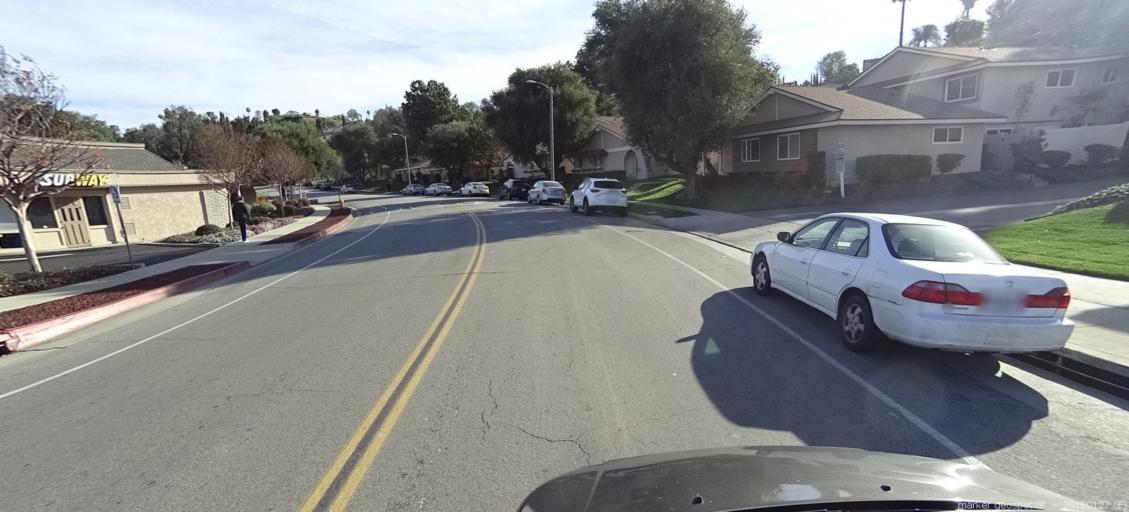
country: US
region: California
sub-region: Los Angeles County
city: Diamond Bar
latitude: 34.0285
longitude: -117.8099
